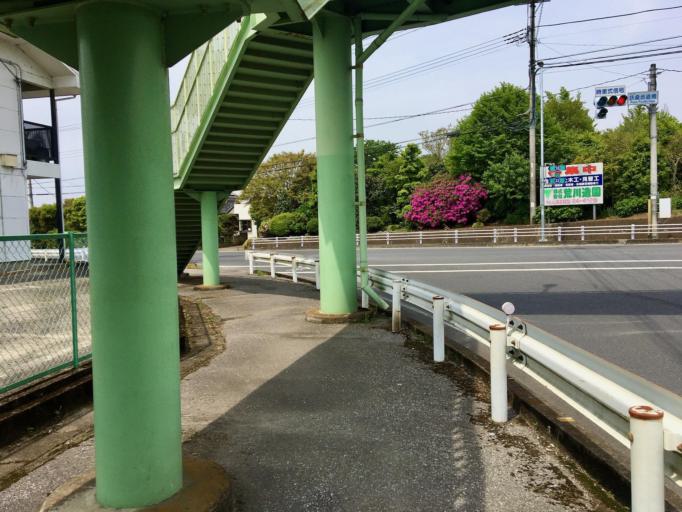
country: JP
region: Tochigi
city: Oyama
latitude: 36.3577
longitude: 139.8134
